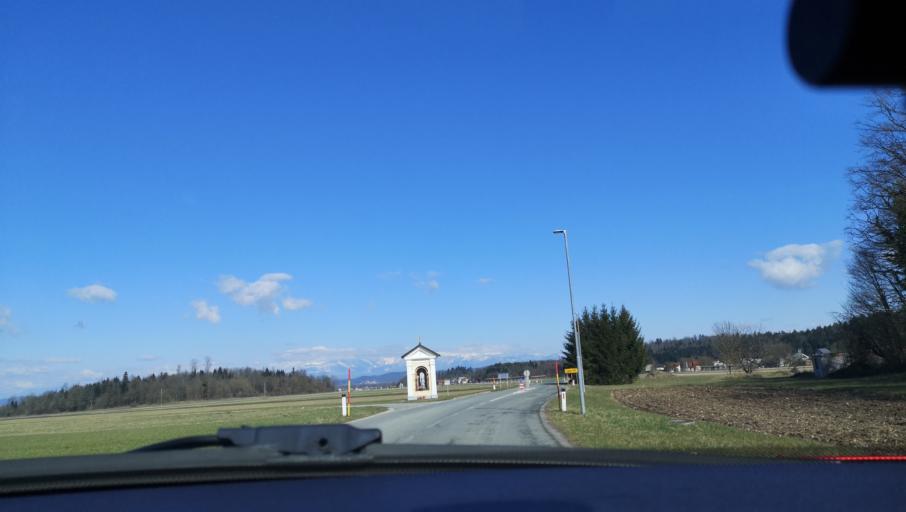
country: SI
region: Ig
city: Ig
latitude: 45.9447
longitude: 14.5095
